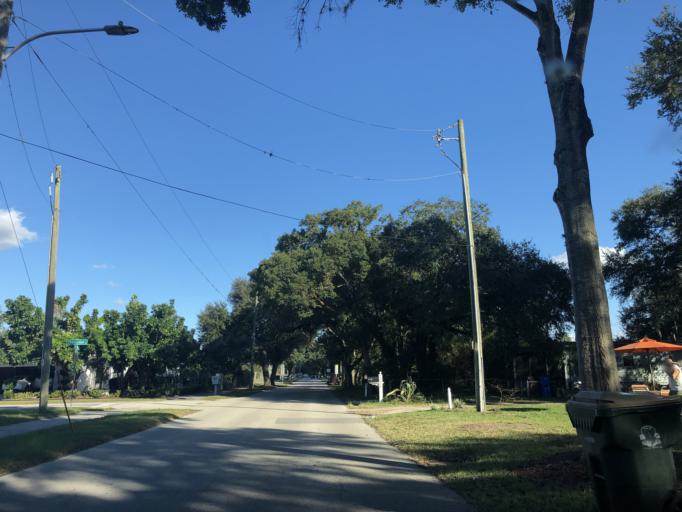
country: US
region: Florida
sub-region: Osceola County
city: Saint Cloud
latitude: 28.2533
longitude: -81.3065
